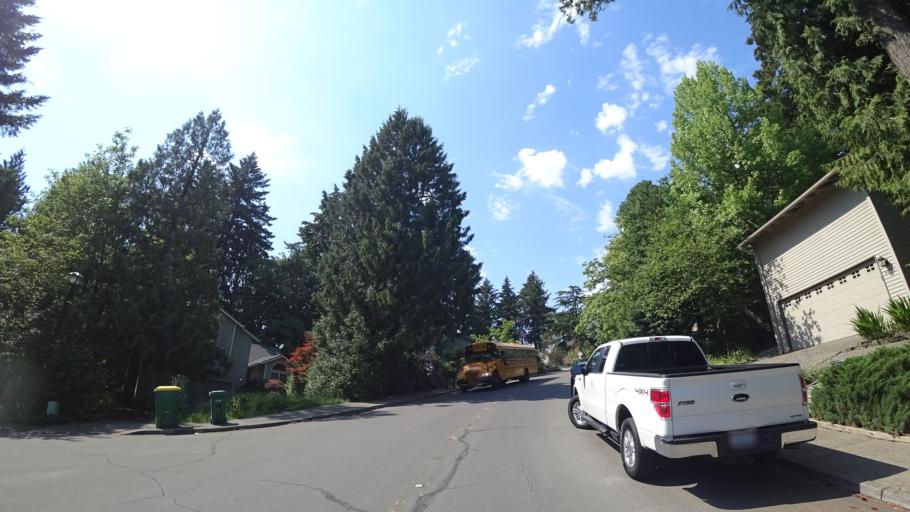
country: US
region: Oregon
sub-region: Washington County
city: Metzger
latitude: 45.4489
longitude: -122.7480
